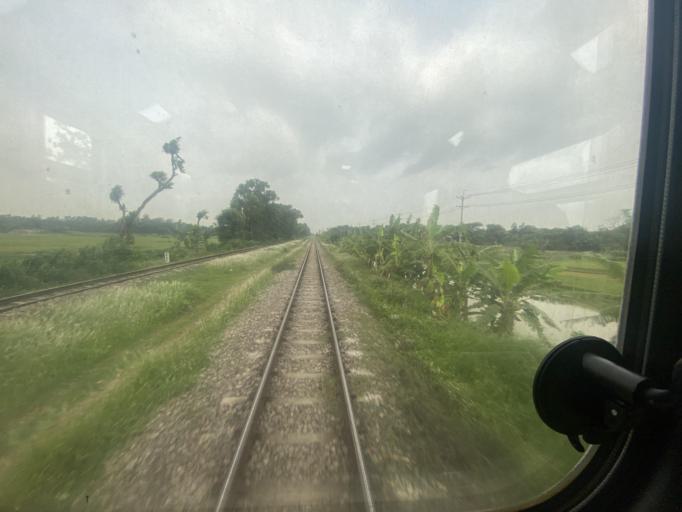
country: BD
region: Dhaka
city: Tungi
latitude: 23.9327
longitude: 90.5149
